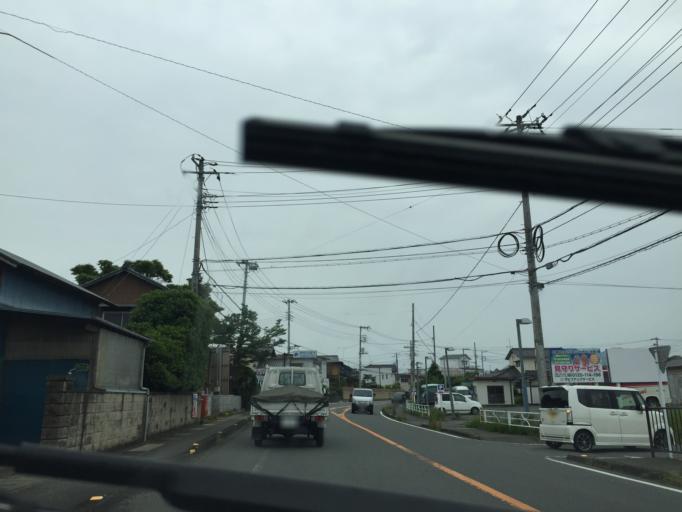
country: JP
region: Shizuoka
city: Mishima
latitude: 35.0672
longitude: 138.9427
